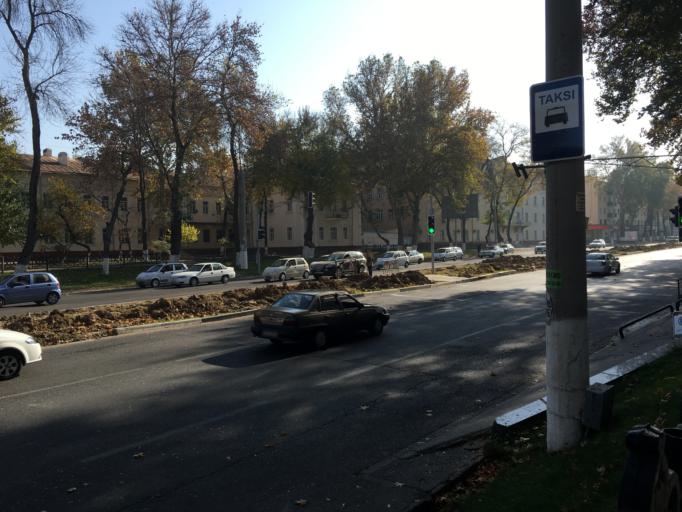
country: UZ
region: Toshkent Shahri
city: Tashkent
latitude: 41.2981
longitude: 69.2494
